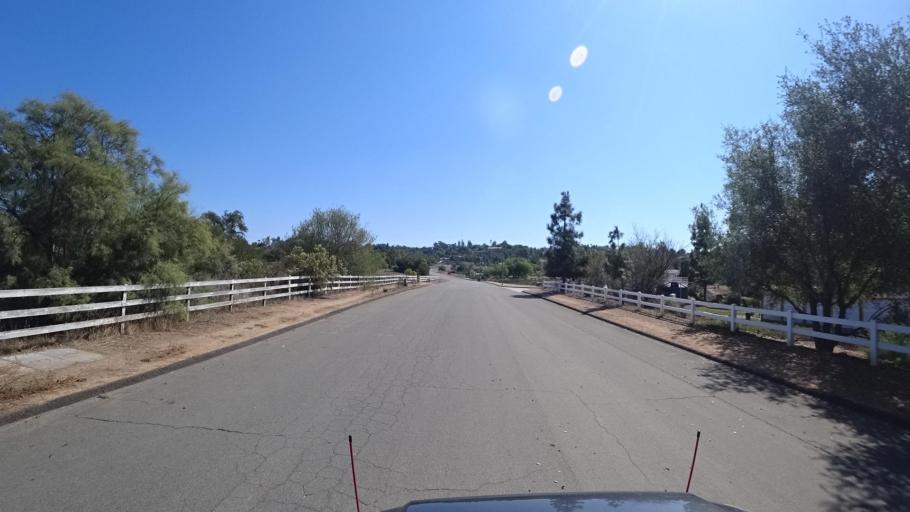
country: US
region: California
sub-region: San Diego County
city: Crest
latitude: 32.8276
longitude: -116.8559
